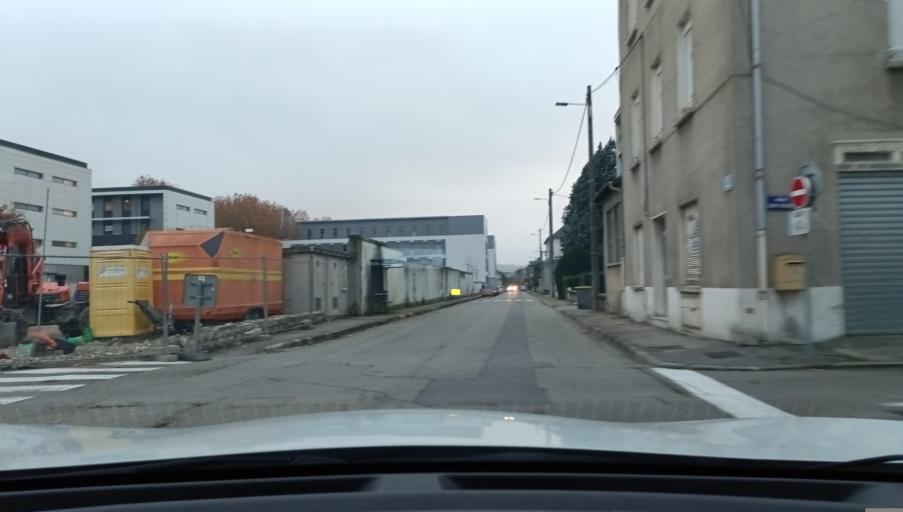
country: FR
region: Rhone-Alpes
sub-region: Departement de l'Isere
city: Vienne
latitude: 45.5154
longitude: 4.8649
